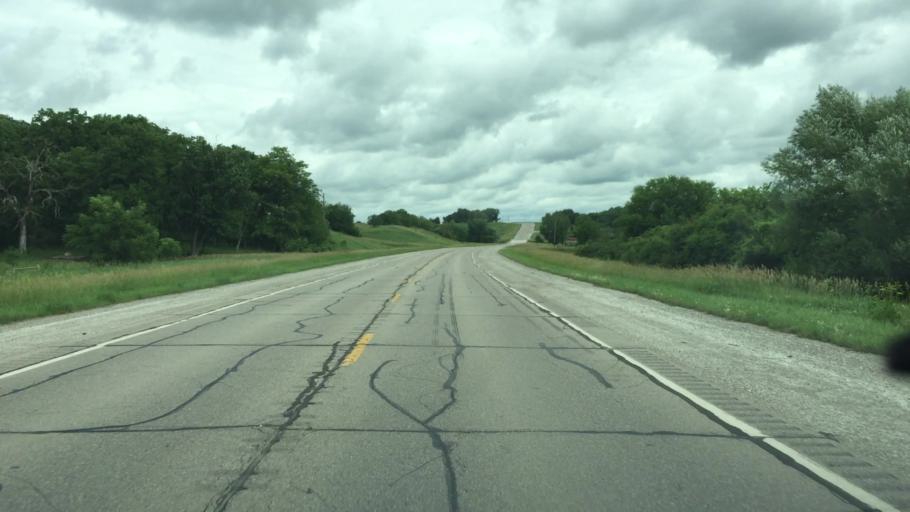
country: US
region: Iowa
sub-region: Jasper County
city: Monroe
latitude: 41.5352
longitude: -93.1015
